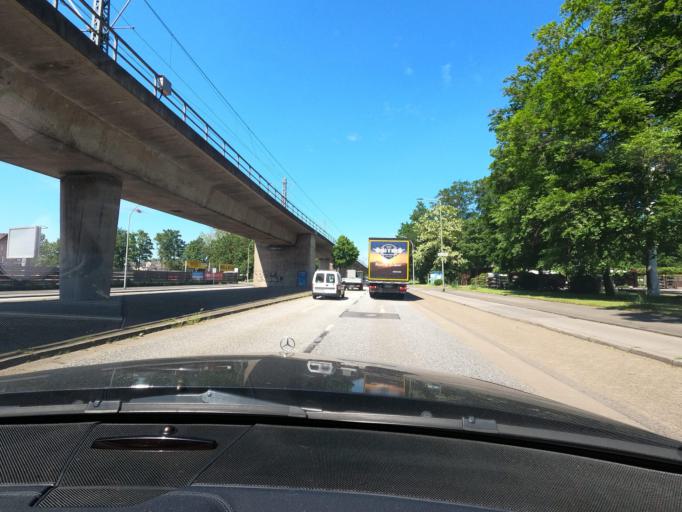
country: DE
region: North Rhine-Westphalia
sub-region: Regierungsbezirk Dusseldorf
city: Hochfeld
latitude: 51.3949
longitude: 6.7597
